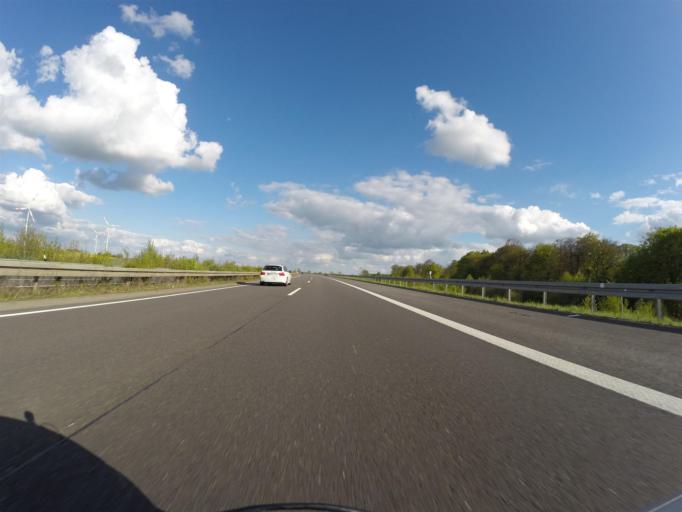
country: DE
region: Saarland
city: Orscholz
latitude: 49.4563
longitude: 6.4804
